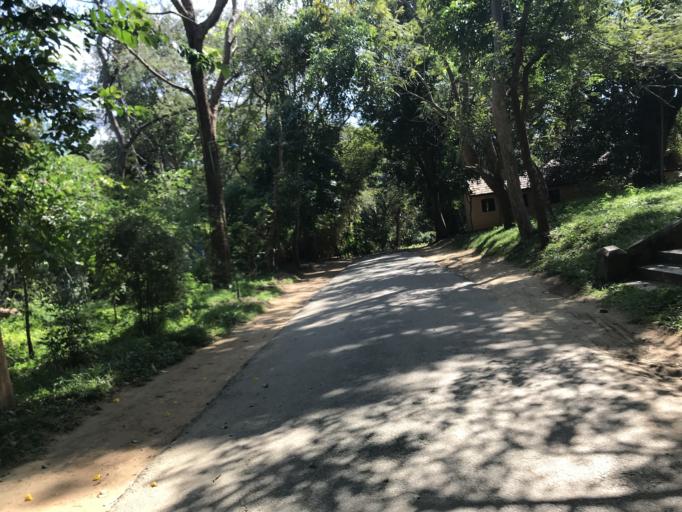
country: IN
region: Karnataka
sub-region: Mysore
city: Sargur
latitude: 11.9383
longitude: 76.2704
